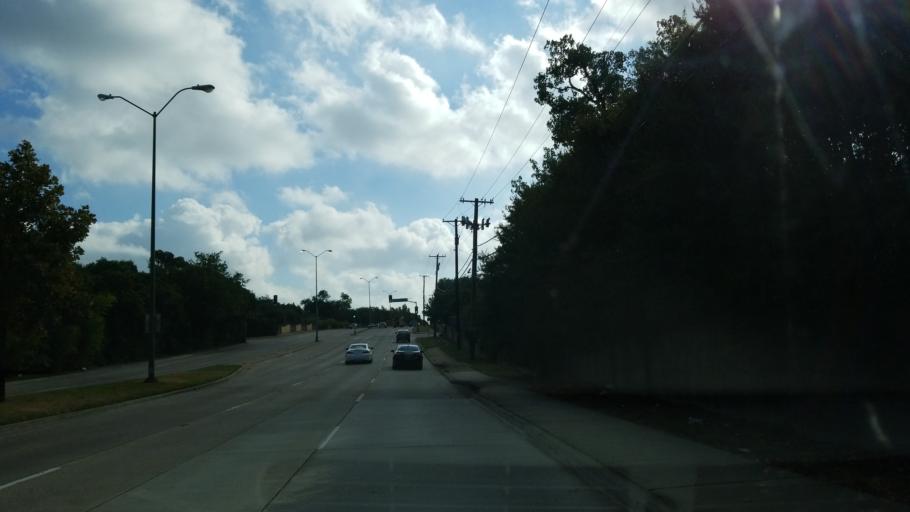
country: US
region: Texas
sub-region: Dallas County
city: Addison
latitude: 32.9499
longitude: -96.7937
